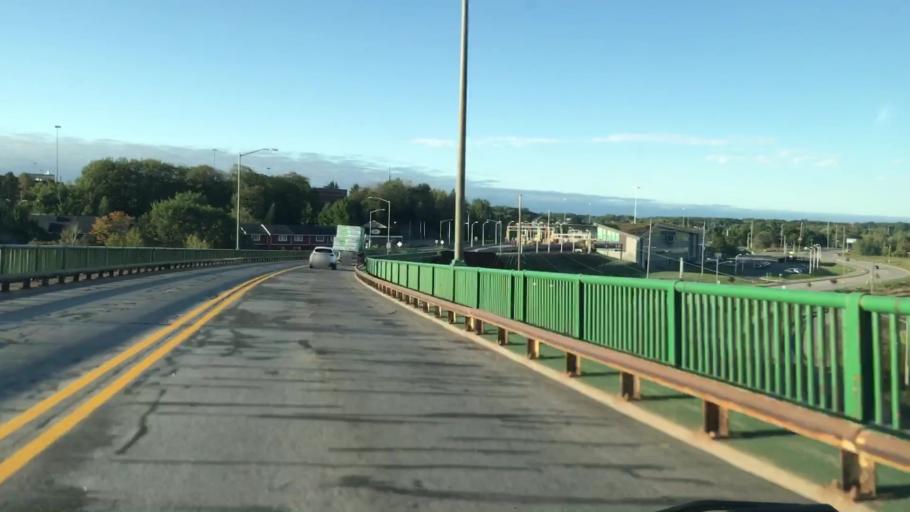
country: US
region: Michigan
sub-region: Chippewa County
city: Sault Ste. Marie
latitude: 46.4975
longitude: -84.3651
